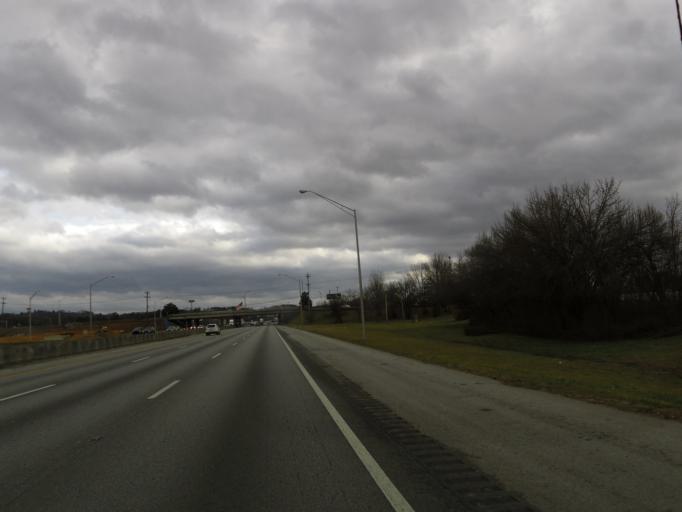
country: US
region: Tennessee
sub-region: Hamilton County
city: East Ridge
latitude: 34.9919
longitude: -85.2053
